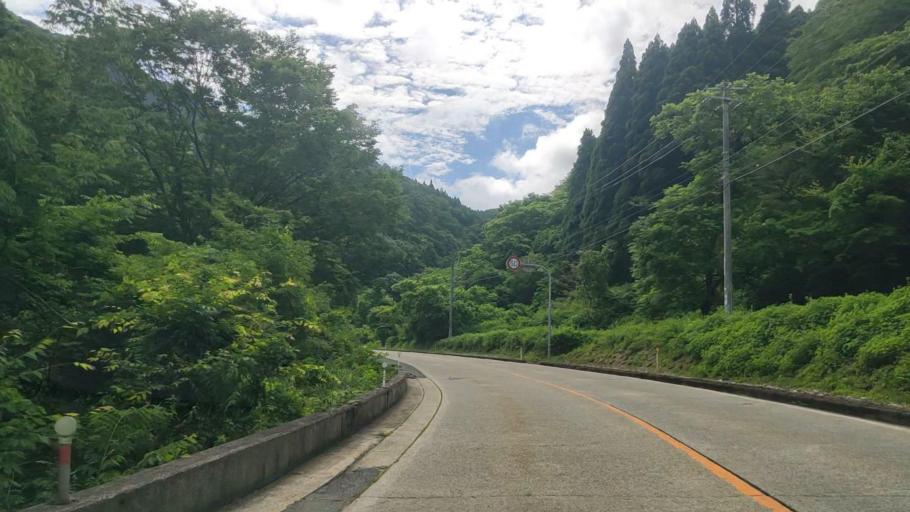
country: JP
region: Okayama
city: Niimi
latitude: 35.2108
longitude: 133.4886
